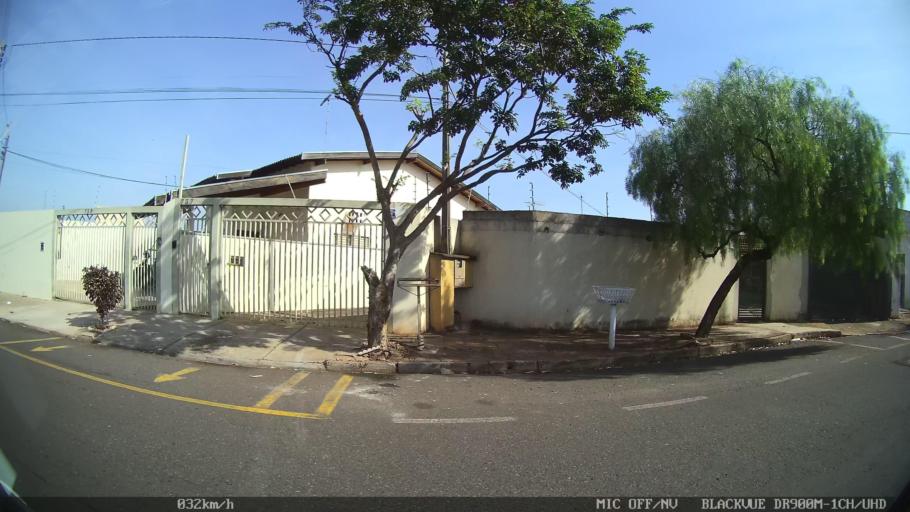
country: BR
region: Sao Paulo
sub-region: Sao Jose Do Rio Preto
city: Sao Jose do Rio Preto
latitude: -20.8003
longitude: -49.4167
